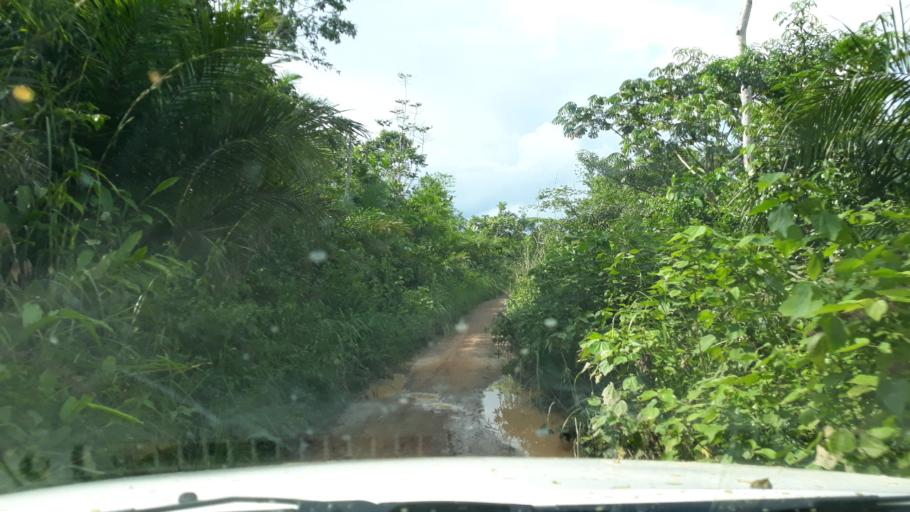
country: CD
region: Maniema
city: Kampene
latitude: -2.7584
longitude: 26.9273
